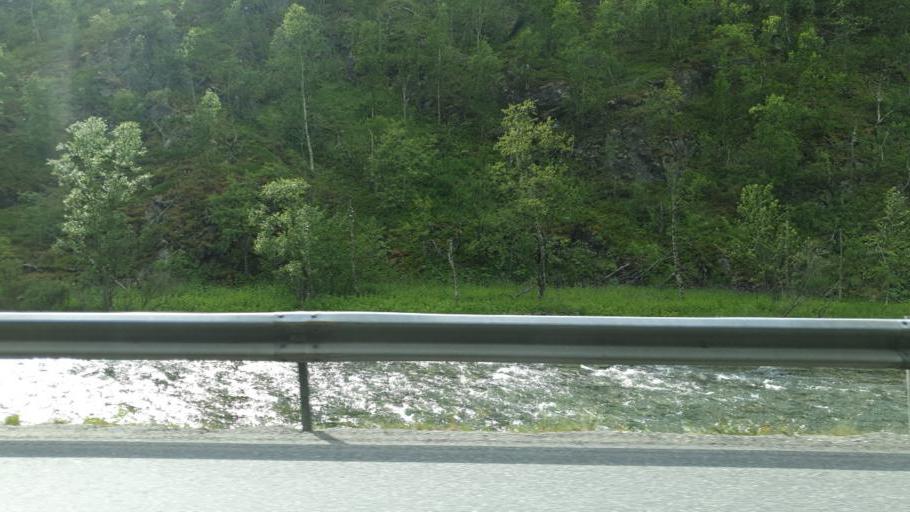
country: NO
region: Sor-Trondelag
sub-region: Oppdal
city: Oppdal
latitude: 62.3613
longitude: 9.6377
